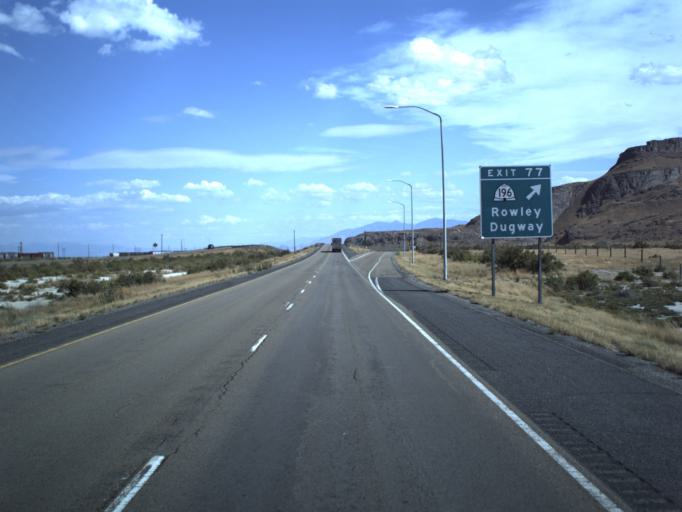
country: US
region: Utah
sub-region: Tooele County
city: Grantsville
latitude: 40.7463
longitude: -112.6602
